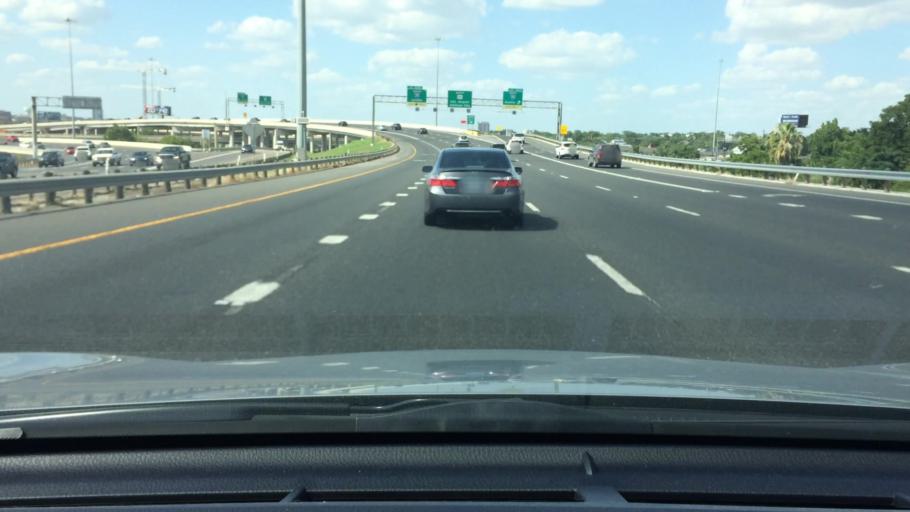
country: US
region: Texas
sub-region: Bexar County
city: San Antonio
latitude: 29.4349
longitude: -98.4773
